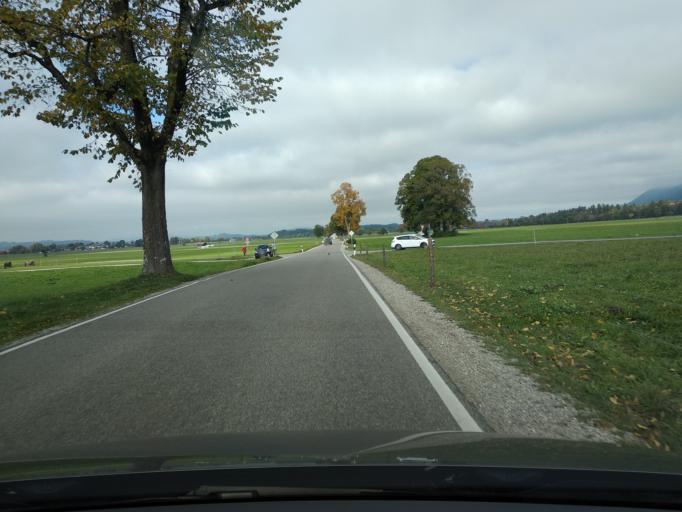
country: DE
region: Bavaria
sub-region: Swabia
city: Schwangau
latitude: 47.5675
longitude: 10.7441
